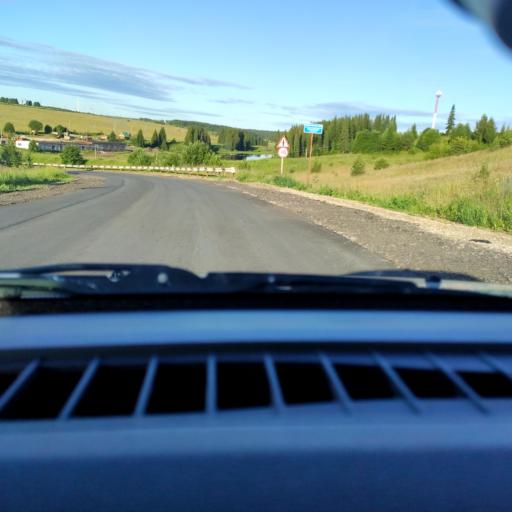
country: RU
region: Perm
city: Uinskoye
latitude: 57.1116
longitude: 56.5325
